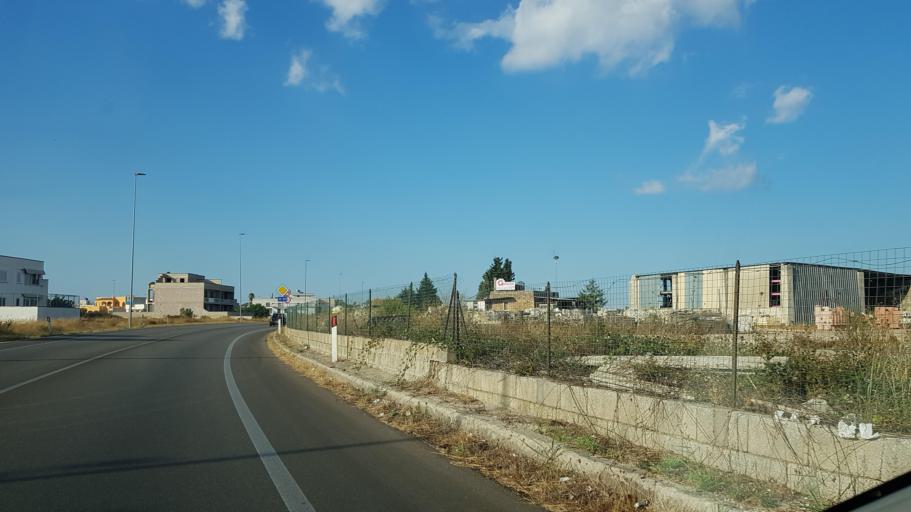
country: IT
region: Apulia
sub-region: Provincia di Lecce
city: Montesano Salentino
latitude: 39.9682
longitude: 18.3233
